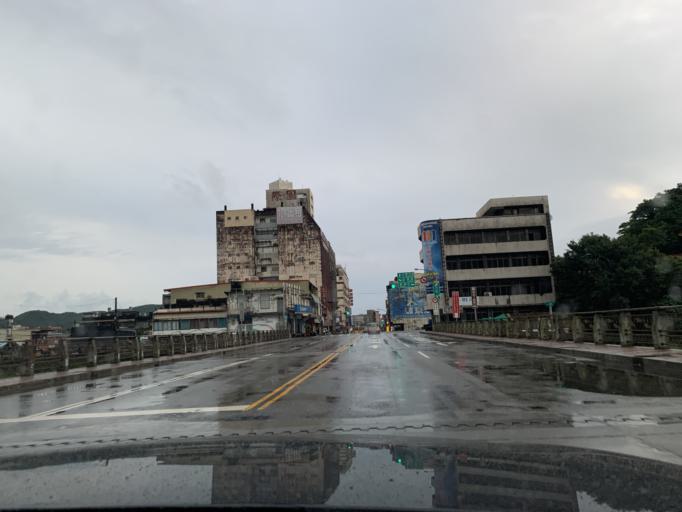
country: TW
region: Taiwan
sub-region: Yilan
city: Yilan
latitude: 24.5962
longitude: 121.8532
